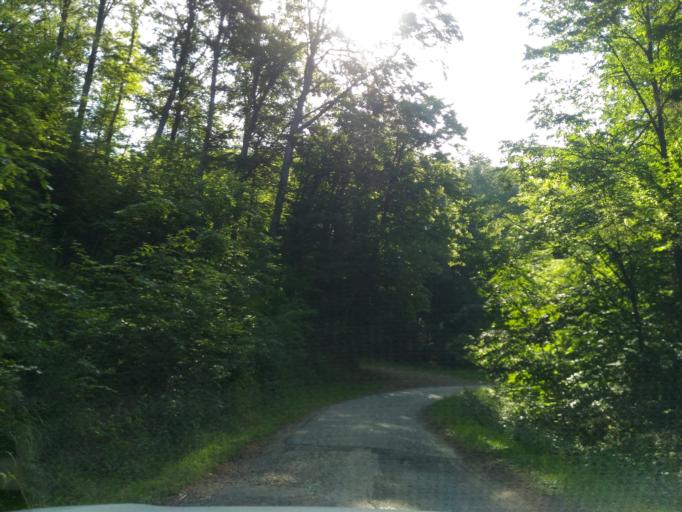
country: HU
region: Baranya
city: Hosszuheteny
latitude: 46.2217
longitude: 18.3444
